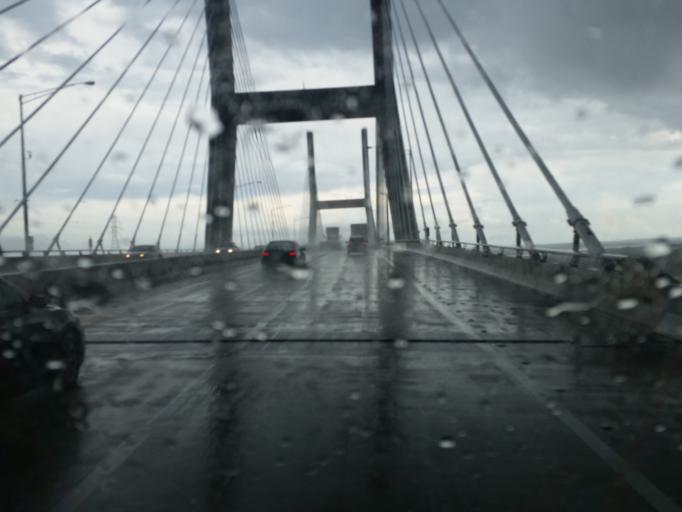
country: US
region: Alabama
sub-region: Mobile County
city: Prichard
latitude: 30.7340
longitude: -88.0451
